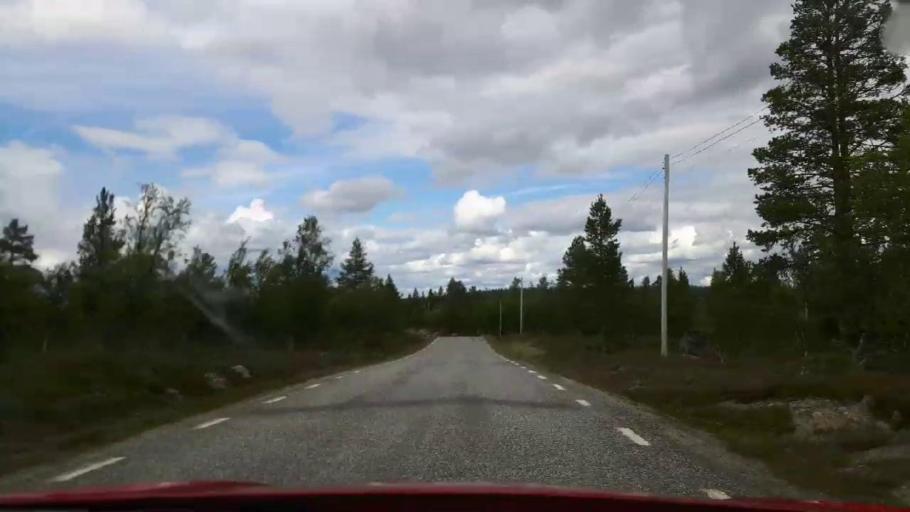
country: NO
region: Hedmark
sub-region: Engerdal
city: Engerdal
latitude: 62.3439
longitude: 12.7974
